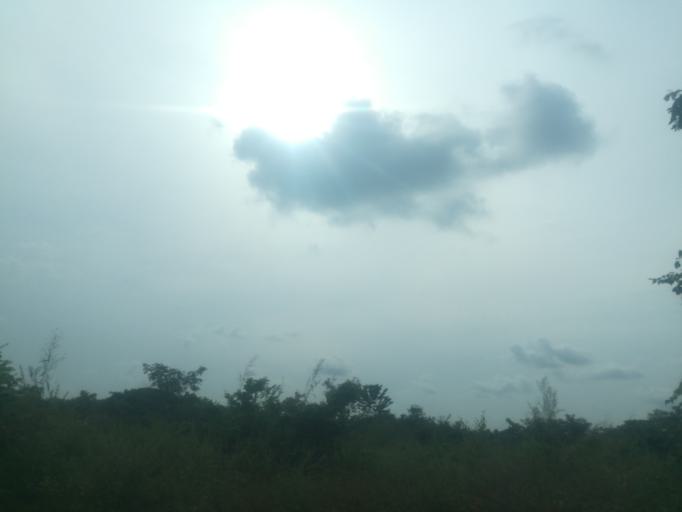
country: NG
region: Ogun
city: Ayetoro
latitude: 7.3041
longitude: 3.0746
